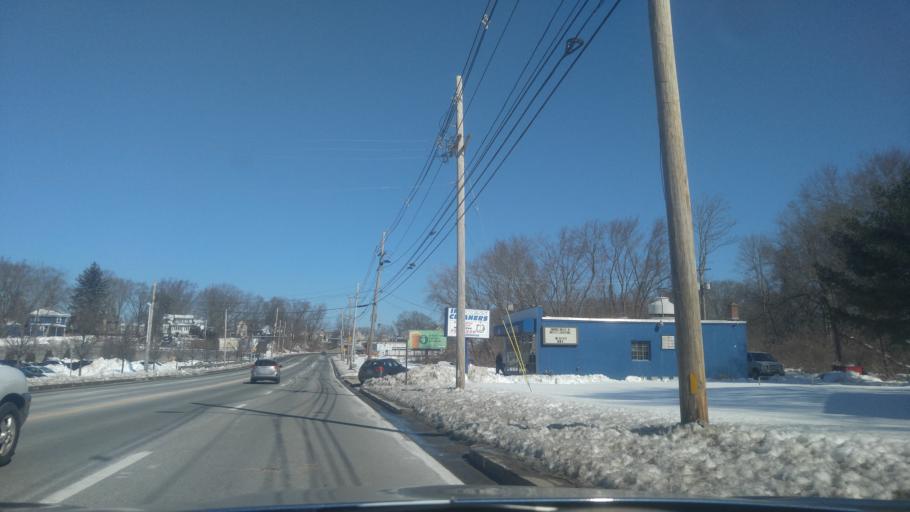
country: US
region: Rhode Island
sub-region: Providence County
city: Cranston
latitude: 41.7686
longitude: -71.4052
